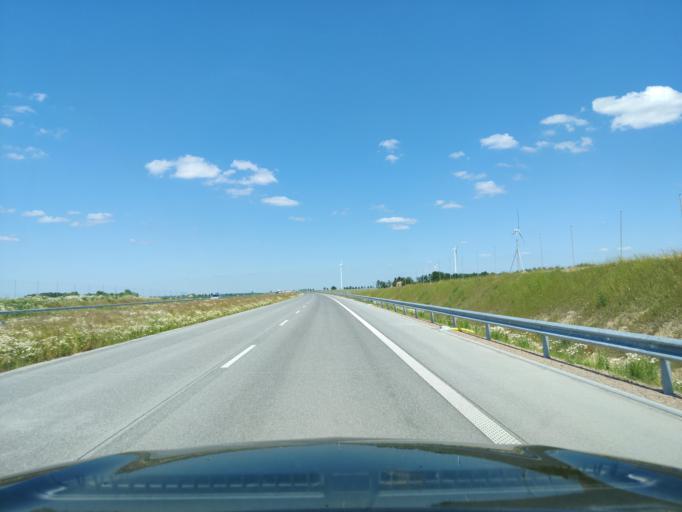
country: PL
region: Masovian Voivodeship
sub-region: Powiat mlawski
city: Wisniewo
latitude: 53.0387
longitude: 20.3560
